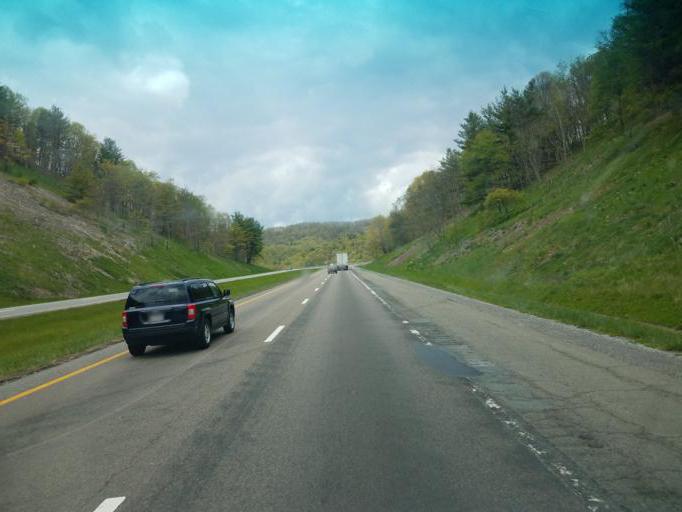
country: US
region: Virginia
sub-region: Wythe County
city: Wytheville
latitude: 37.0116
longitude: -81.1041
